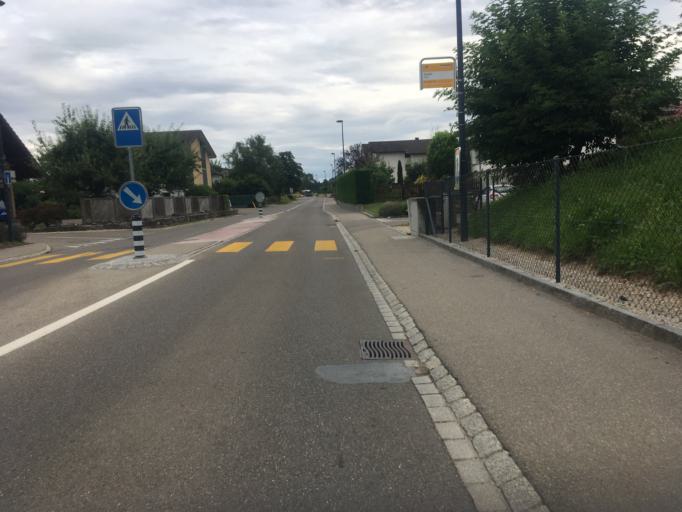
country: CH
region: Bern
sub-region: Seeland District
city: Erlach
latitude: 47.0398
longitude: 7.0966
